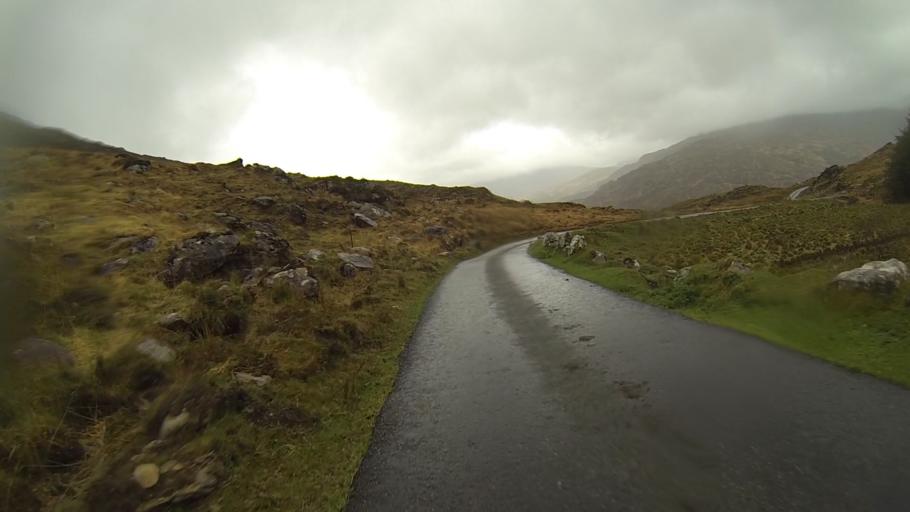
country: IE
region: Munster
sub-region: Ciarrai
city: Kenmare
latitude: 51.9923
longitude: -9.6431
